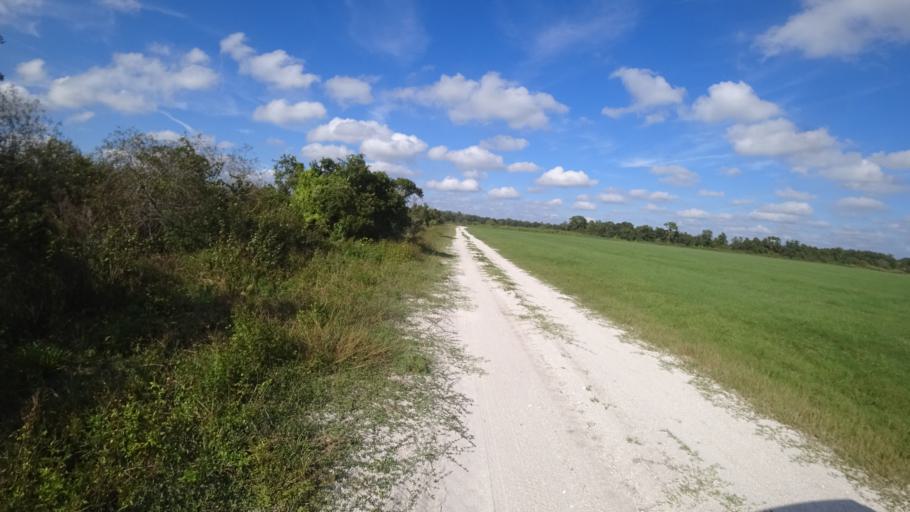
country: US
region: Florida
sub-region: Sarasota County
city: Lake Sarasota
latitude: 27.3704
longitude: -82.1575
